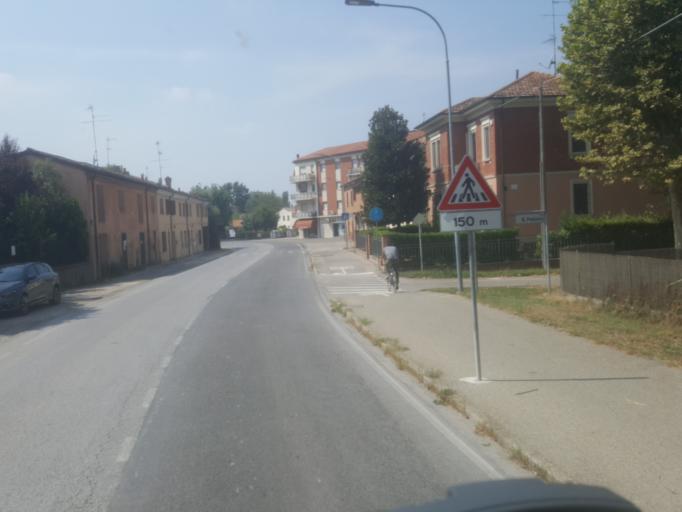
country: IT
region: Emilia-Romagna
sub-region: Provincia di Ravenna
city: Lavezzola
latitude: 44.5666
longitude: 11.8750
